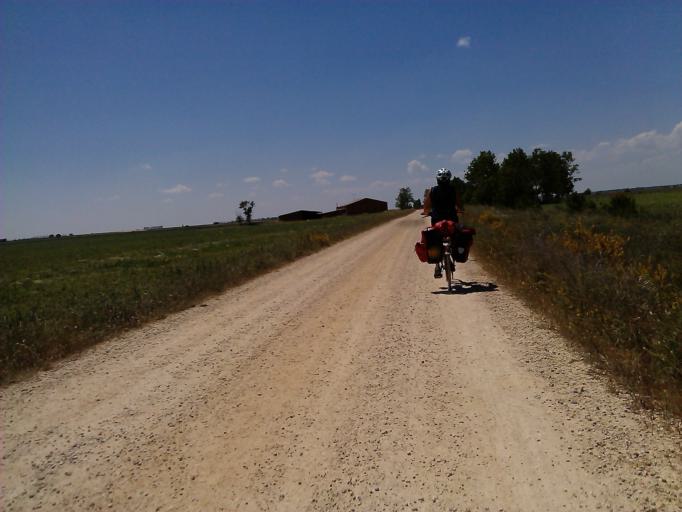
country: ES
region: Castille and Leon
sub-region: Provincia de Palencia
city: Bustillo del Paramo de Carrion
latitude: 42.3388
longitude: -4.7141
